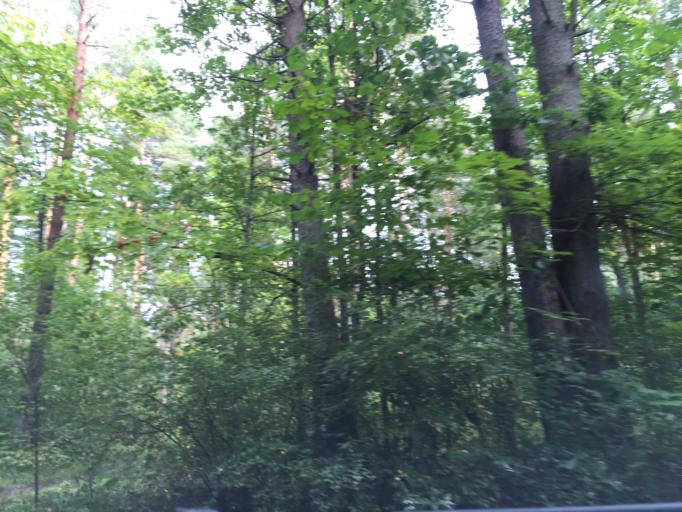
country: LV
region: Ikskile
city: Ikskile
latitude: 56.8270
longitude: 24.5100
